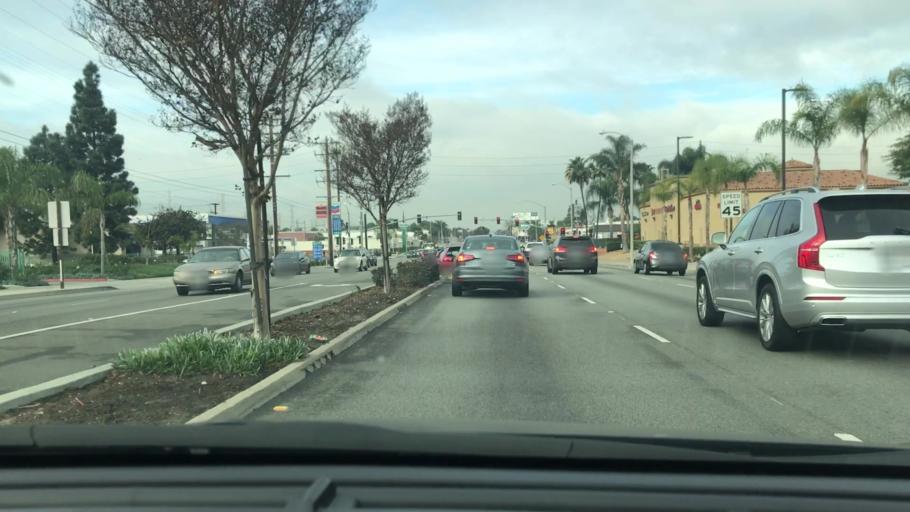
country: US
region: California
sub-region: Los Angeles County
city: Gardena
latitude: 33.8729
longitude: -118.3076
